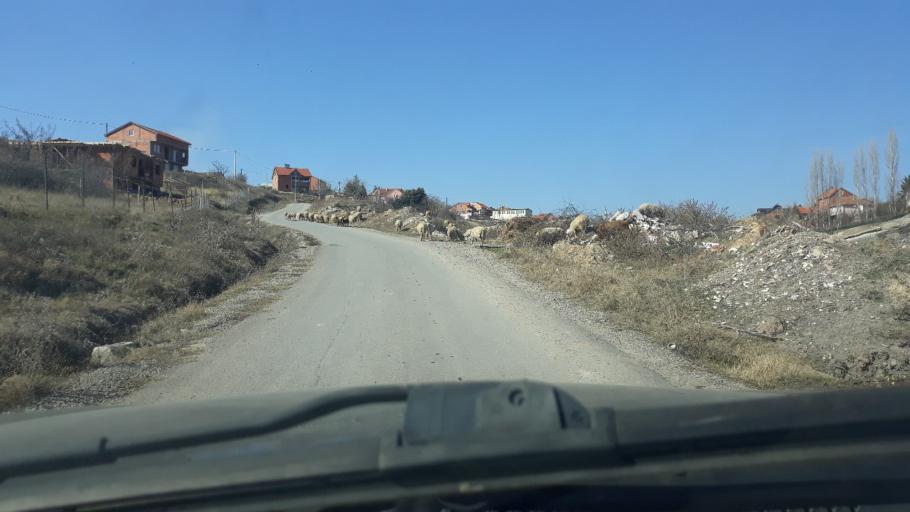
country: MK
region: Veles
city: Gorno Orizari
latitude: 41.6801
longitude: 21.7367
